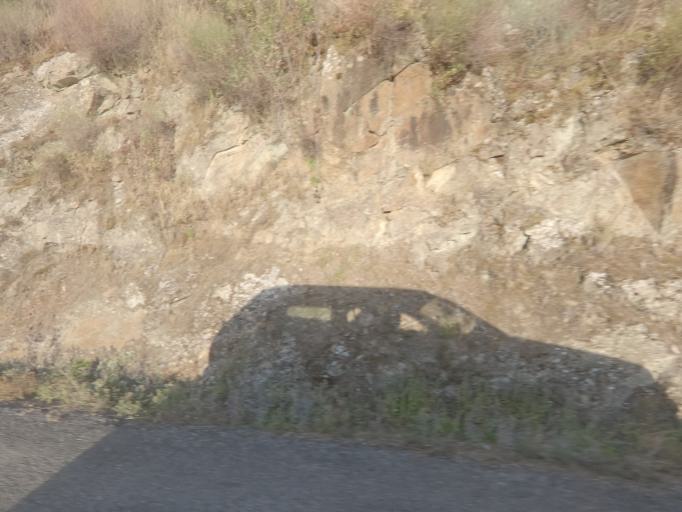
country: PT
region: Viseu
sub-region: Armamar
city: Armamar
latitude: 41.1748
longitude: -7.6917
